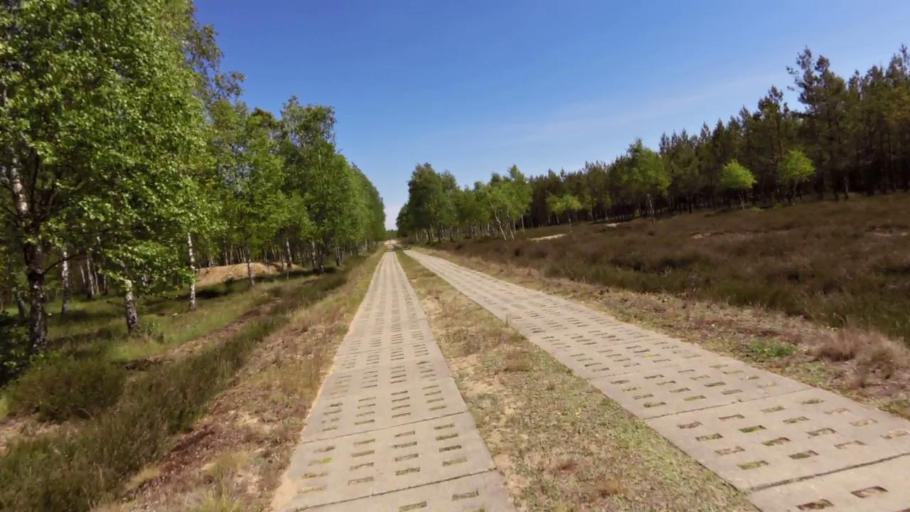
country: PL
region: West Pomeranian Voivodeship
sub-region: Powiat szczecinecki
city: Borne Sulinowo
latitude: 53.5707
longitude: 16.6310
